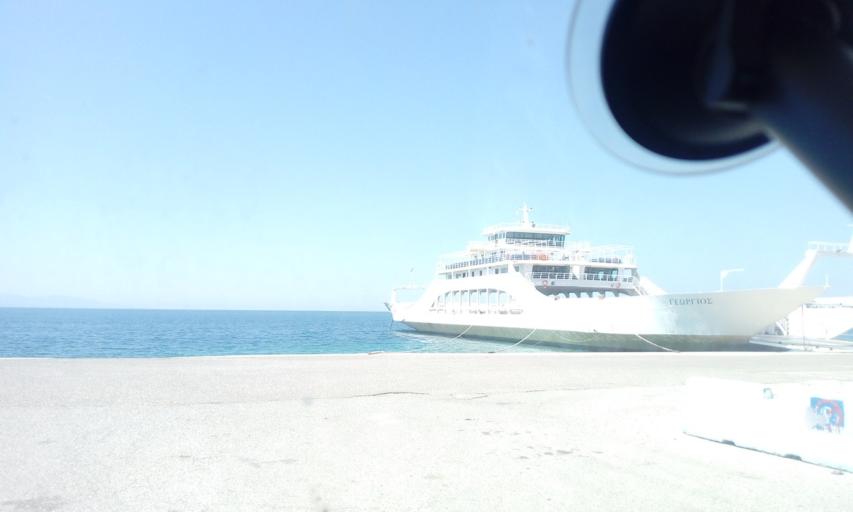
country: GR
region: West Greece
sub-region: Nomos Aitolias kai Akarnanias
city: Antirrio
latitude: 38.3290
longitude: 21.7640
